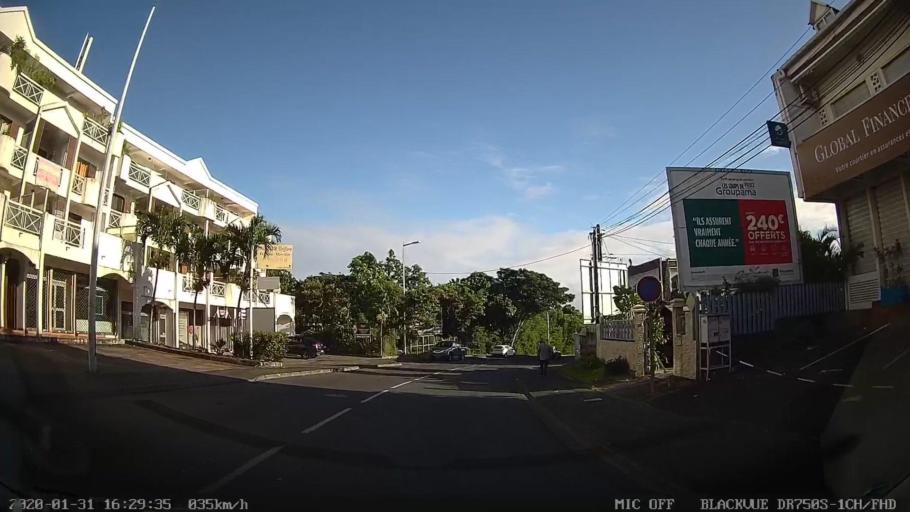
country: RE
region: Reunion
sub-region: Reunion
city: Saint-Denis
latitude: -20.8974
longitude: 55.4914
